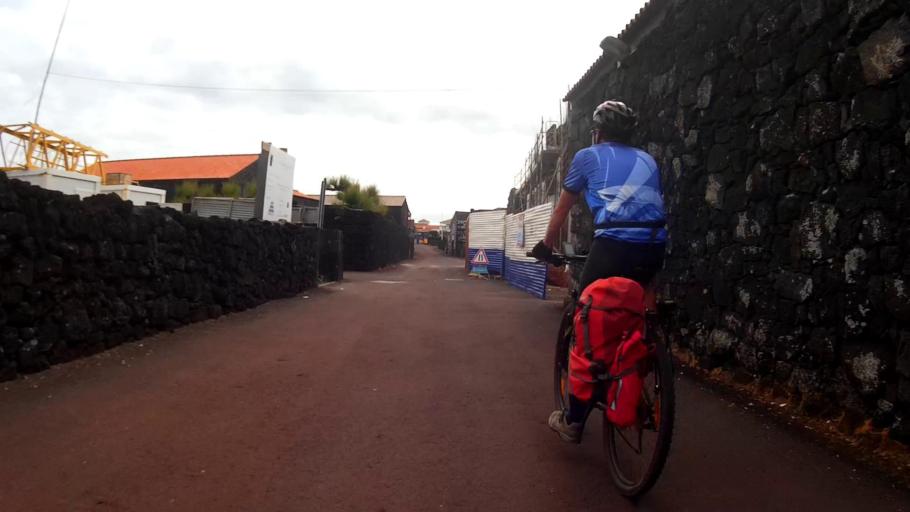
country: PT
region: Azores
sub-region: Madalena
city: Madalena
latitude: 38.5571
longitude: -28.4277
